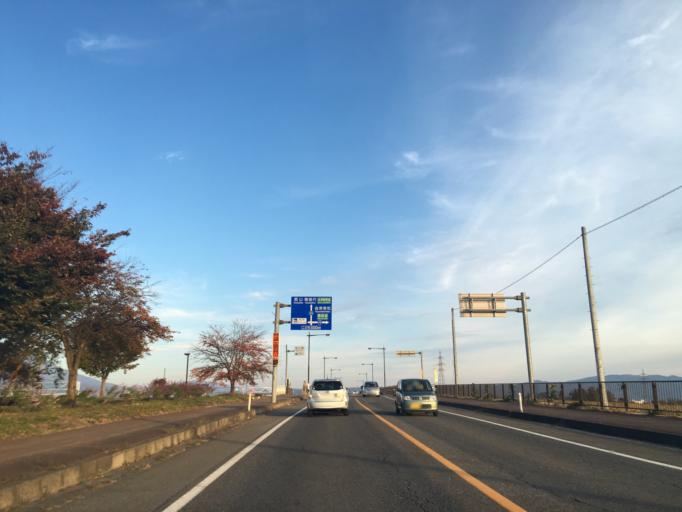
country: JP
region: Fukushima
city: Kitakata
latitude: 37.5571
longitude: 139.8570
